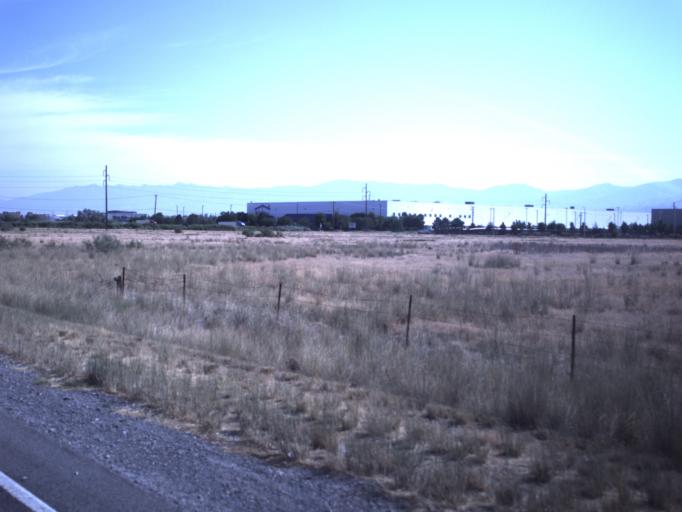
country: US
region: Utah
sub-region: Salt Lake County
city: West Valley City
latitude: 40.7596
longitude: -112.0250
